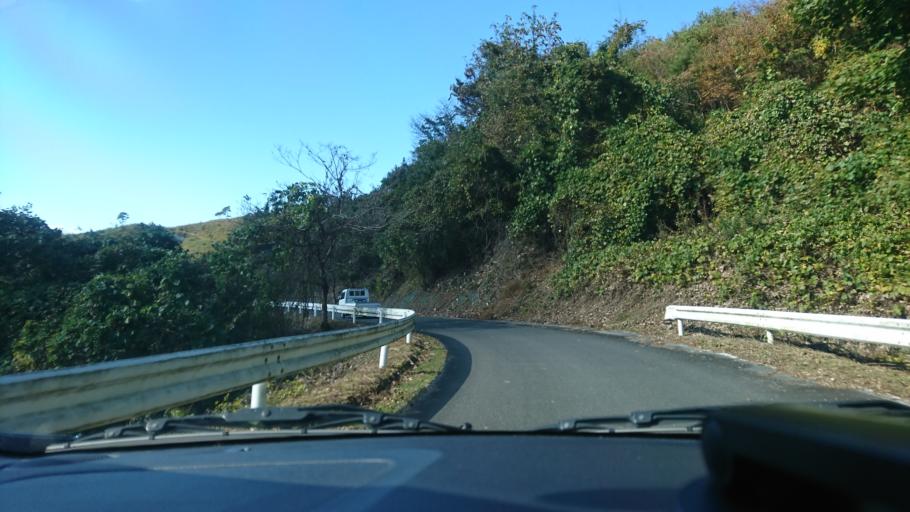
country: JP
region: Iwate
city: Ichinoseki
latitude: 38.7982
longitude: 141.2913
